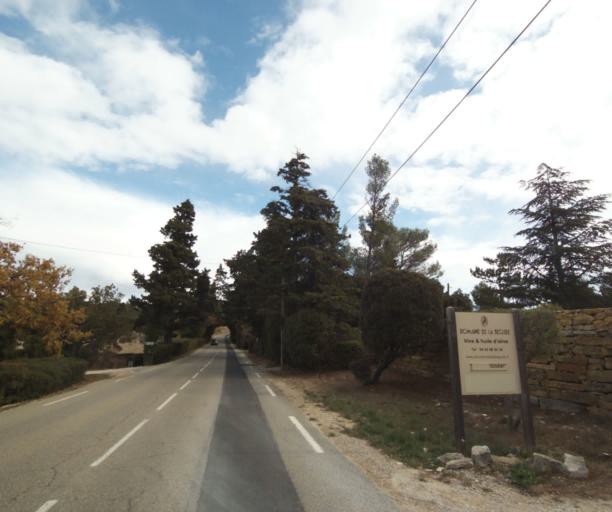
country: FR
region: Provence-Alpes-Cote d'Azur
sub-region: Departement des Bouches-du-Rhone
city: Cuges-les-Pins
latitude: 43.2416
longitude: 5.7024
